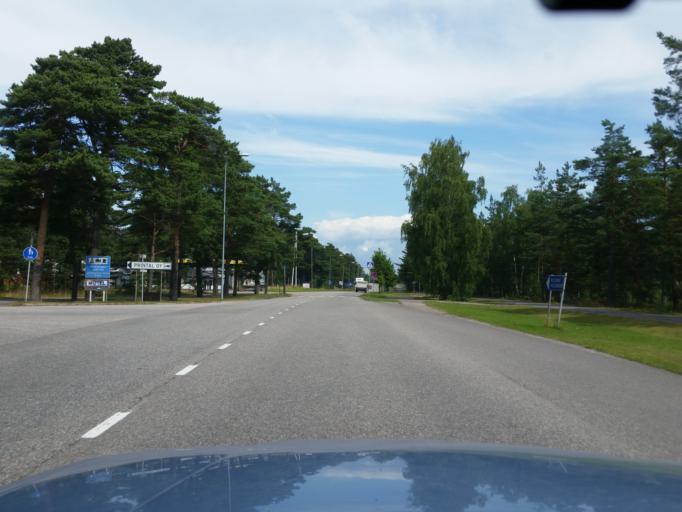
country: FI
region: Uusimaa
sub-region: Raaseporin
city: Hanko
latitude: 59.8376
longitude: 22.9946
